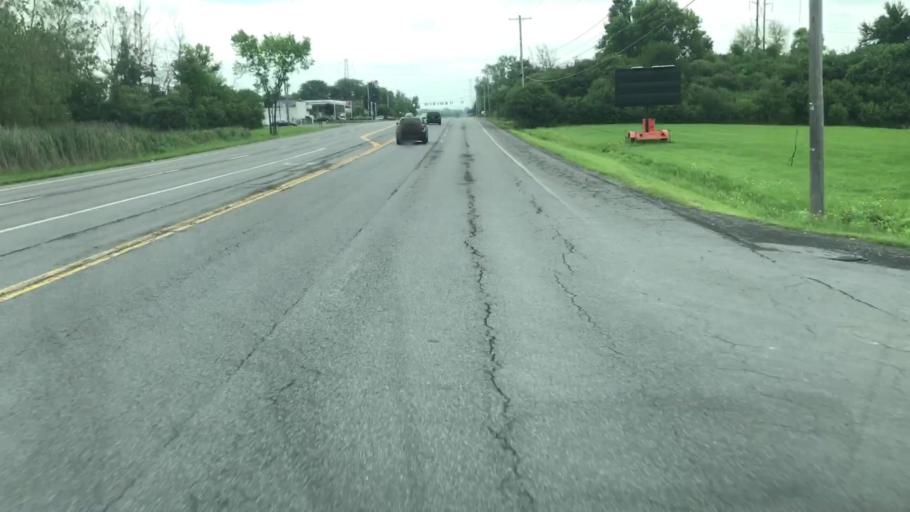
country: US
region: New York
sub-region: Onondaga County
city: Galeville
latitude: 43.1215
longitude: -76.1860
